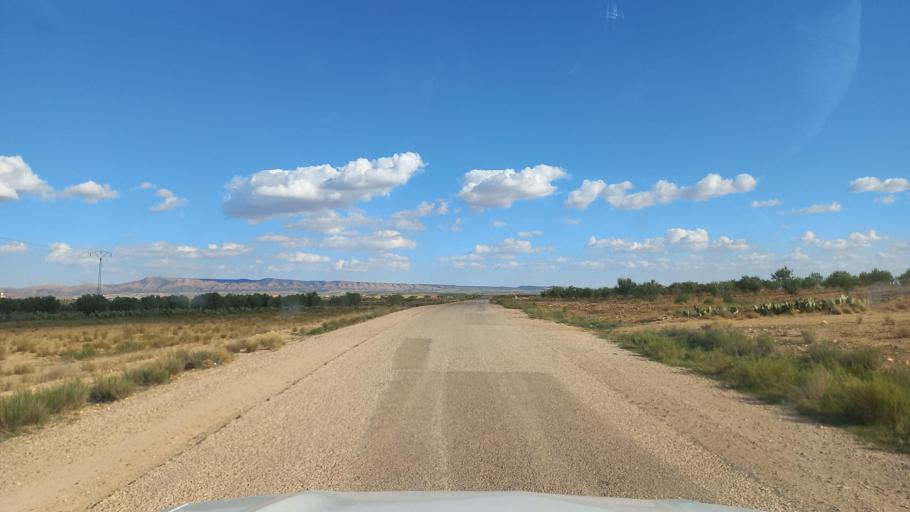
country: TN
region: Al Qasrayn
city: Sbiba
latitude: 35.3918
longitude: 9.0244
